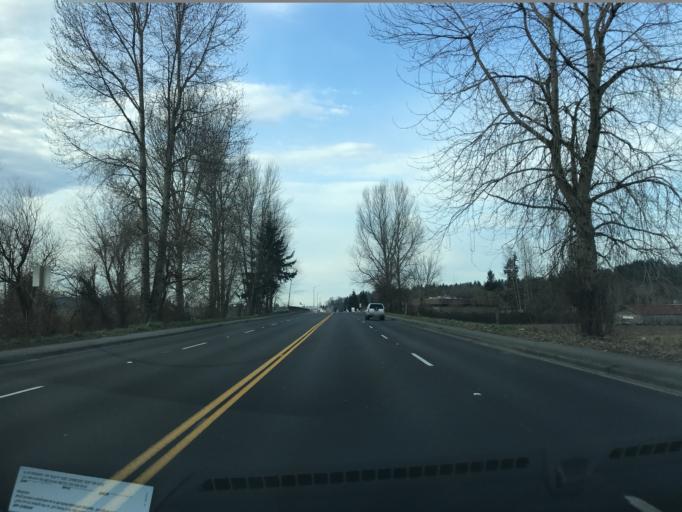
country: US
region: Washington
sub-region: King County
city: Kent
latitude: 47.3595
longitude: -122.2298
